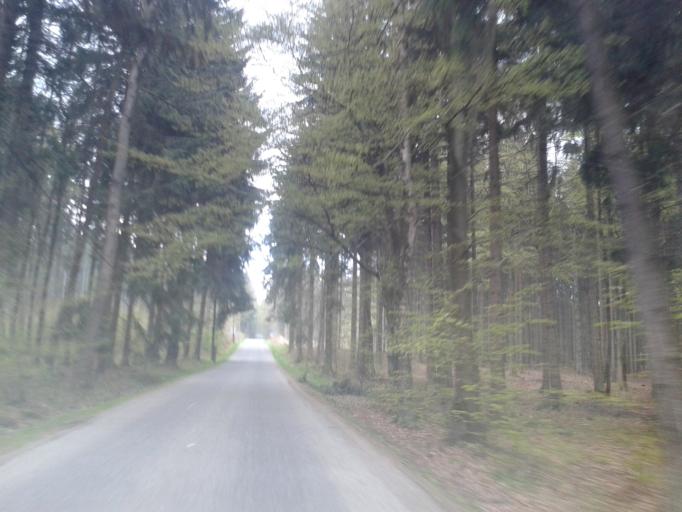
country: CZ
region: Plzensky
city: Zbiroh
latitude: 49.9163
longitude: 13.8235
